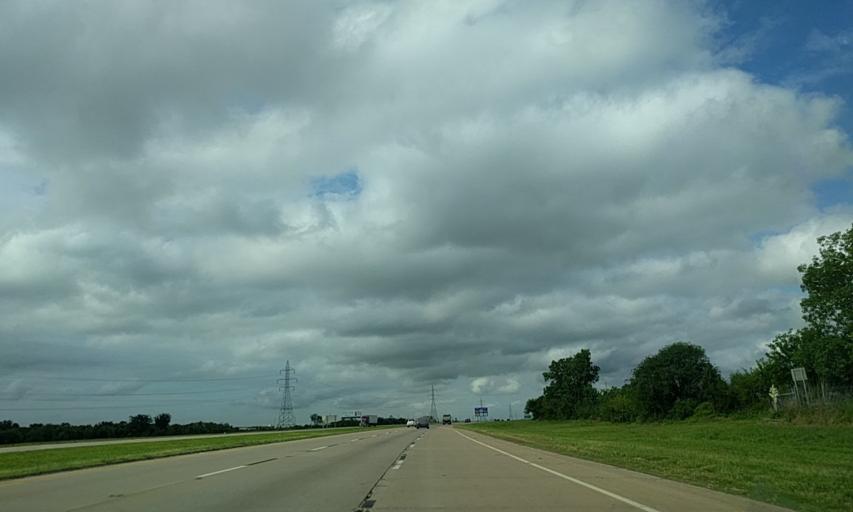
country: US
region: Oklahoma
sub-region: Tulsa County
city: Owasso
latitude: 36.3038
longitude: -95.8231
